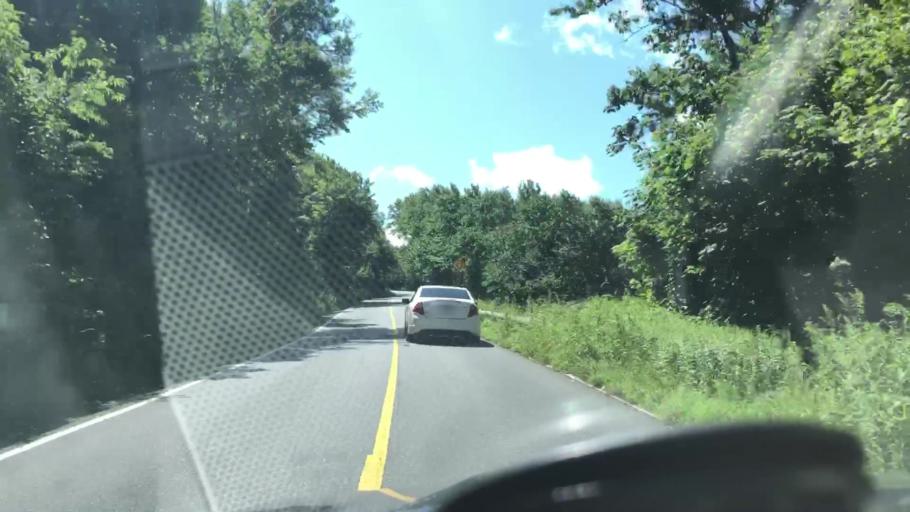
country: US
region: Massachusetts
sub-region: Berkshire County
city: Adams
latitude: 42.6323
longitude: -73.1776
